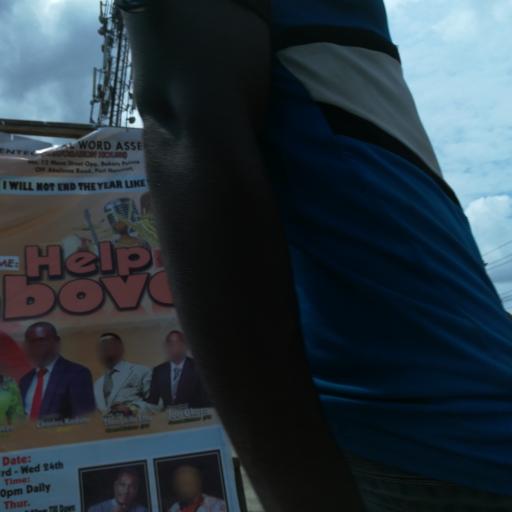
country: NG
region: Rivers
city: Port Harcourt
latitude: 4.7840
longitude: 7.0387
